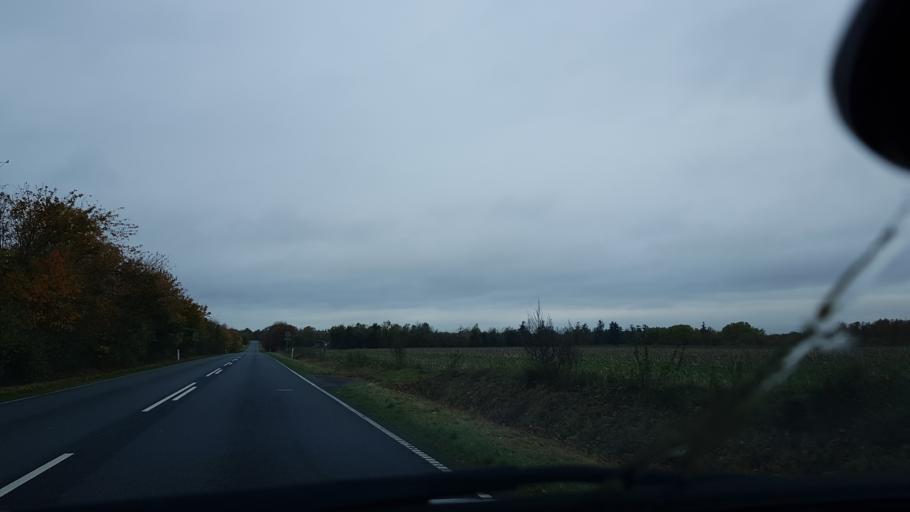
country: DK
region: South Denmark
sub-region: Esbjerg Kommune
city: Ribe
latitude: 55.2876
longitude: 8.8300
